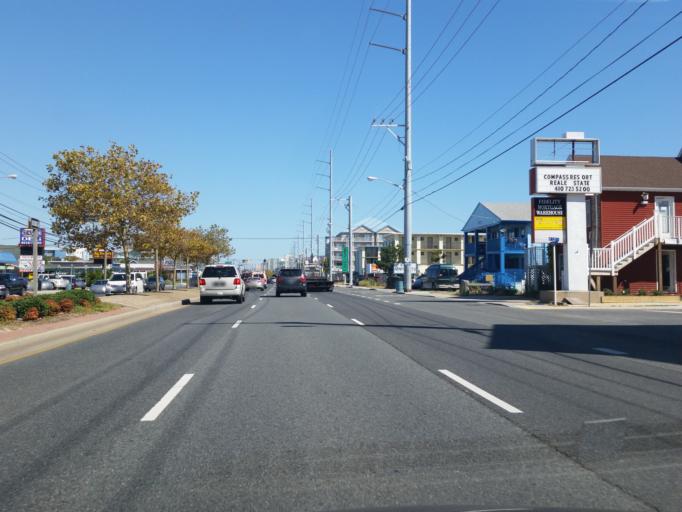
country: US
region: Maryland
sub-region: Worcester County
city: Ocean City
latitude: 38.3928
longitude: -75.0638
